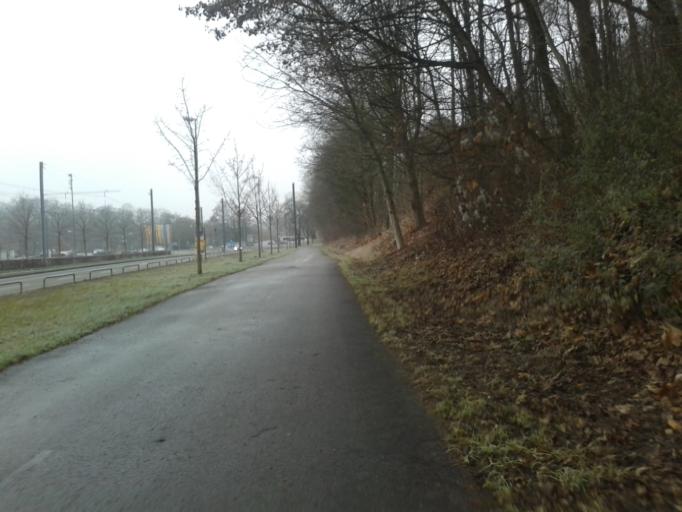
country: DE
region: Bavaria
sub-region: Swabia
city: Neu-Ulm
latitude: 48.4138
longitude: 10.0111
